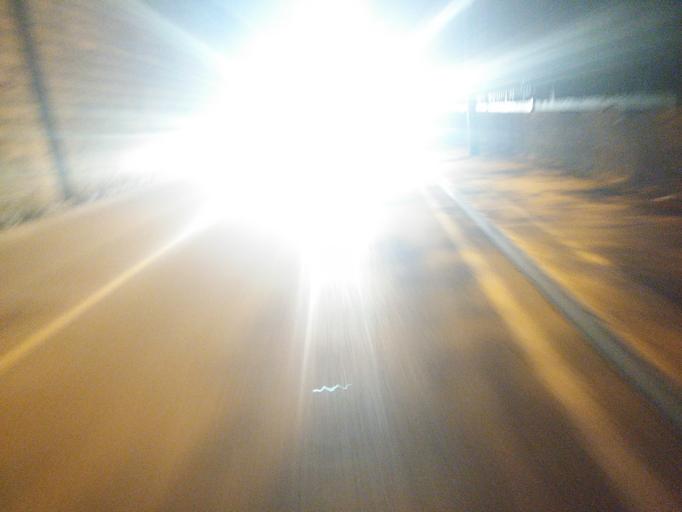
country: IT
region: Apulia
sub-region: Provincia di Bari
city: Modugno
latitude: 41.0894
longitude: 16.7883
